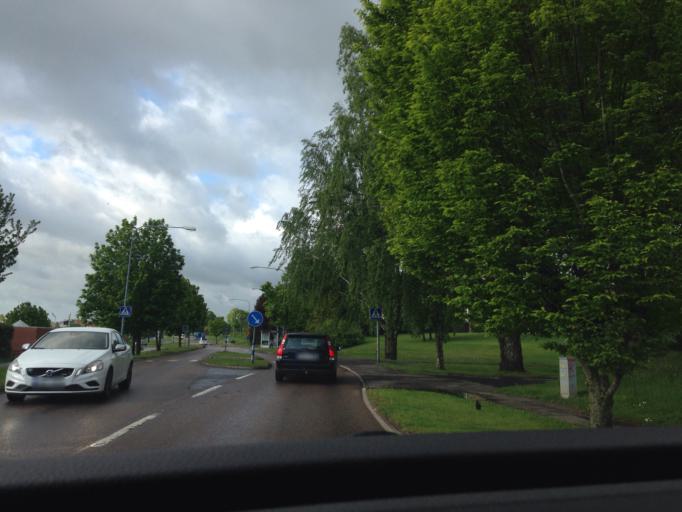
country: SE
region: Vaestra Goetaland
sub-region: Skovde Kommun
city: Skoevde
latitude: 58.4091
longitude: 13.8658
